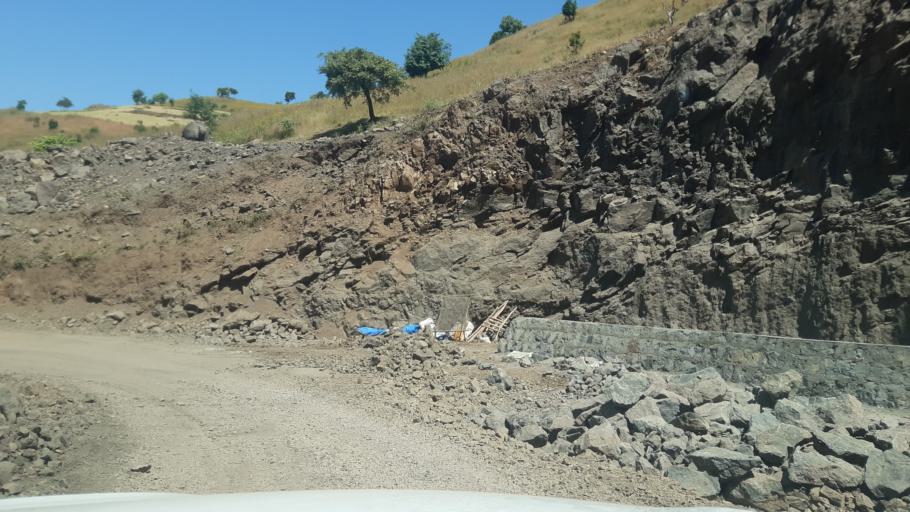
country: ET
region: Amhara
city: Dabat
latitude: 13.1690
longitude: 37.6061
